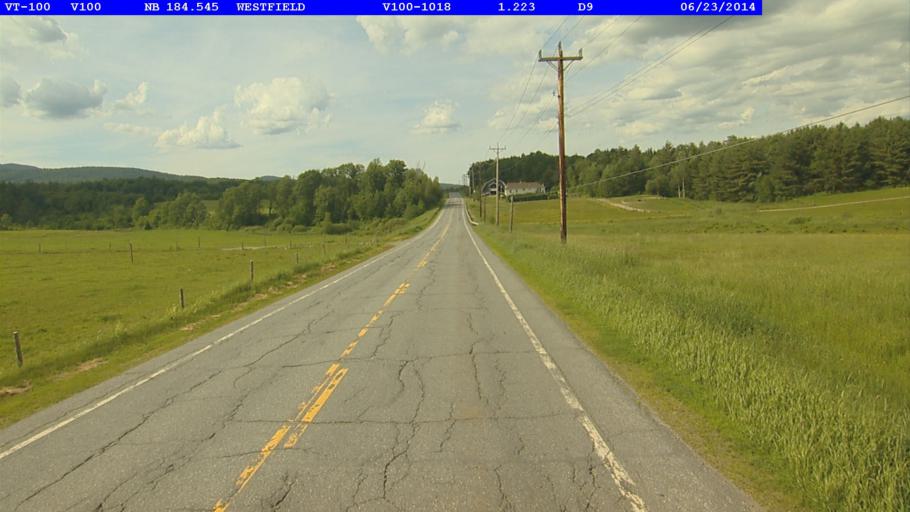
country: US
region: Vermont
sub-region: Orleans County
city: Newport
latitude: 44.8525
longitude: -72.4341
